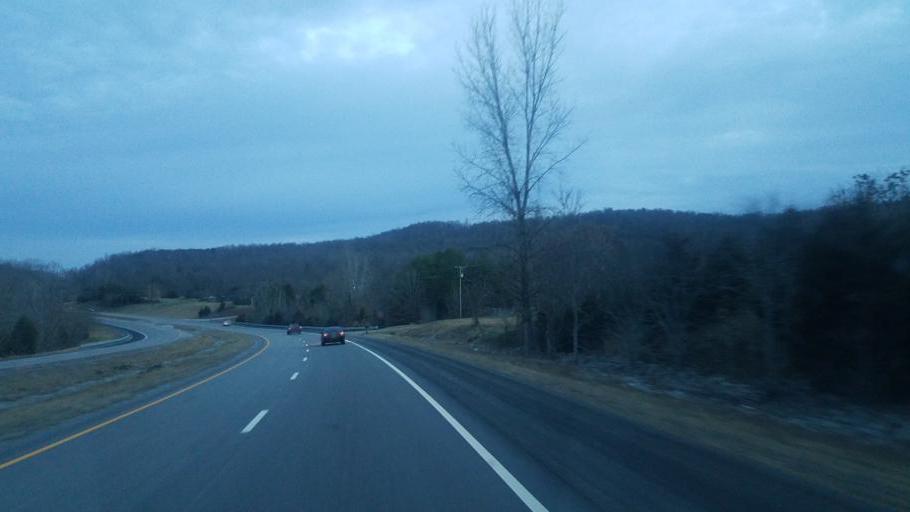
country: US
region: Tennessee
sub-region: White County
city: Sparta
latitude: 35.8584
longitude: -85.4667
